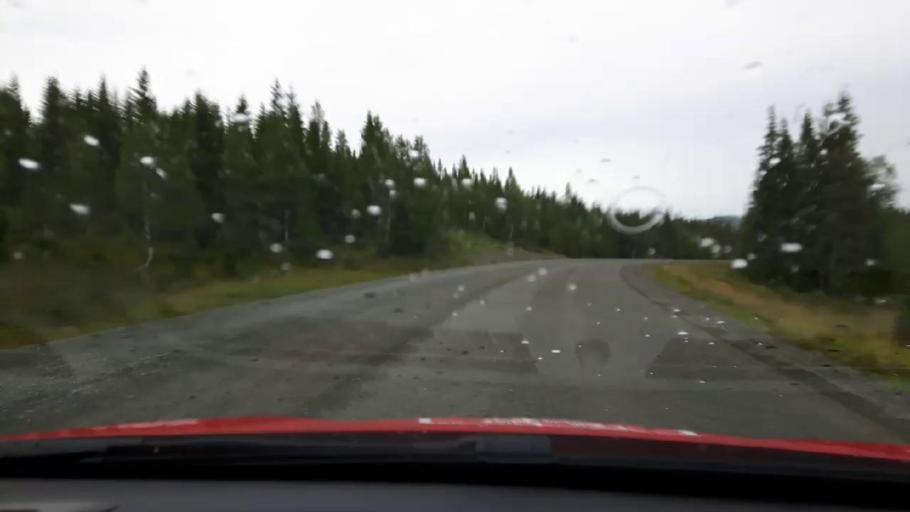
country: SE
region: Jaemtland
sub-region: Are Kommun
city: Are
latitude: 63.4147
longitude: 12.7662
